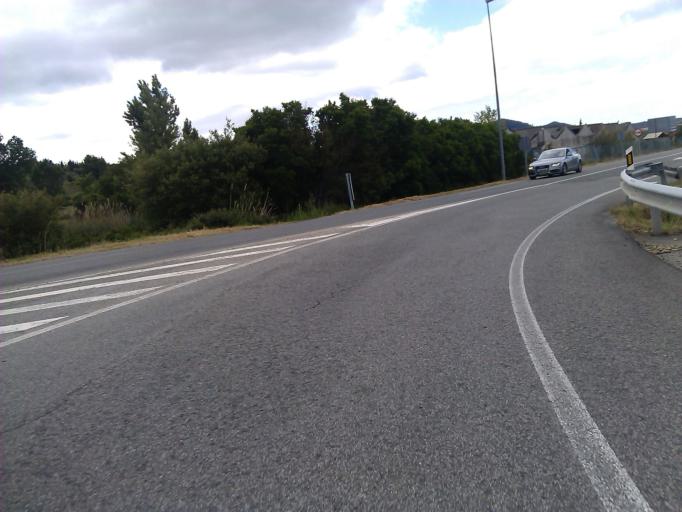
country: ES
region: Navarre
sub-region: Provincia de Navarra
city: Obanos
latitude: 42.6936
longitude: -1.7911
